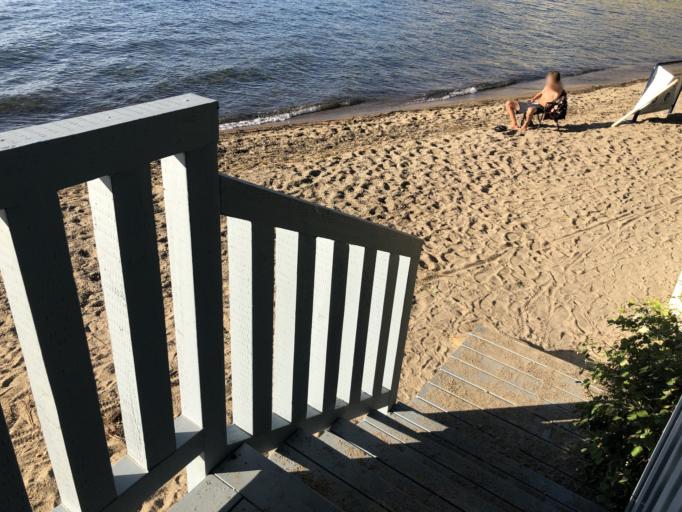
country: CA
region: British Columbia
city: Penticton
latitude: 49.5380
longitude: -119.5758
